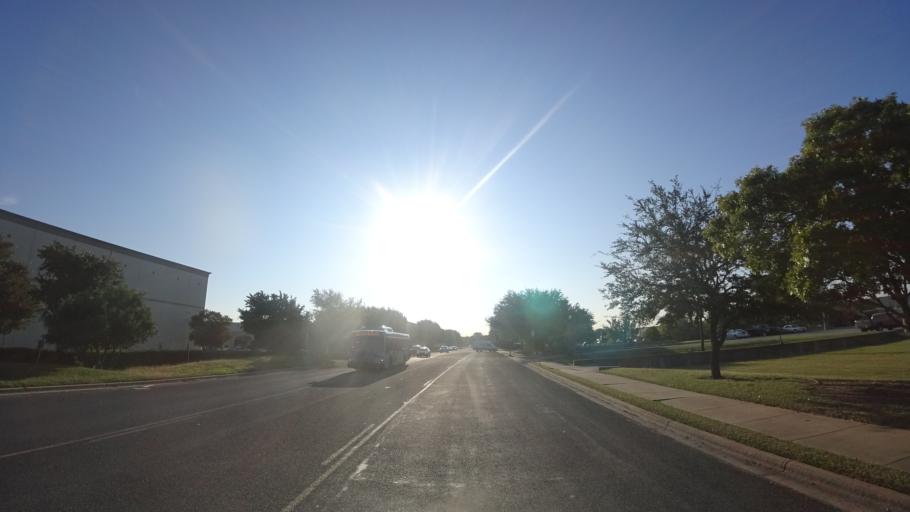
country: US
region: Texas
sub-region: Travis County
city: Manor
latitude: 30.3378
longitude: -97.6612
